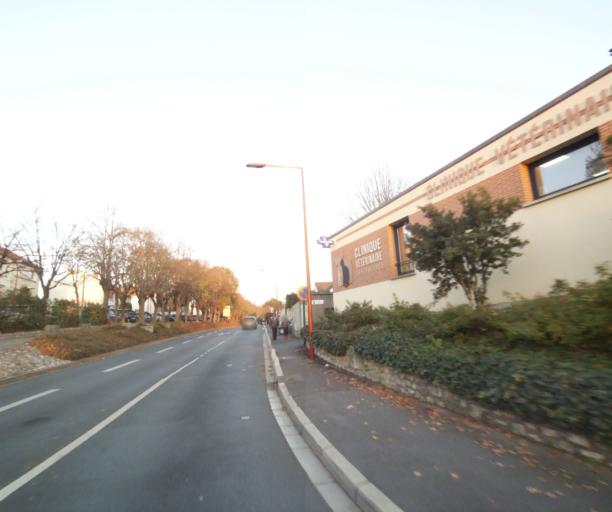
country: FR
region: Ile-de-France
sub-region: Departement du Val-d'Oise
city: Gonesse
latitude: 48.9861
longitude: 2.4380
